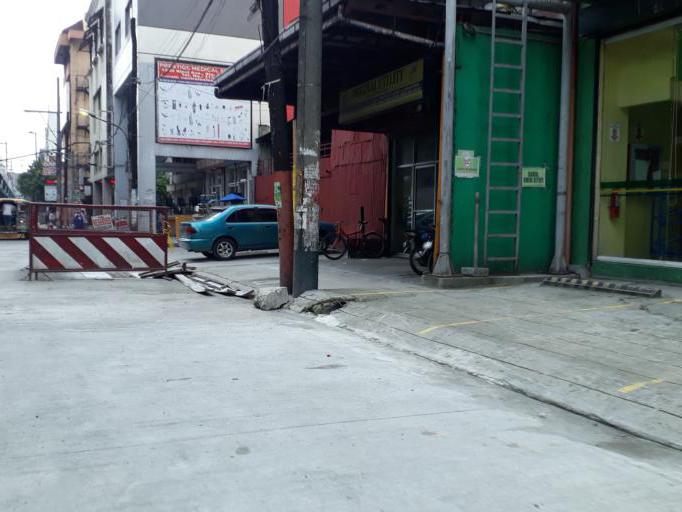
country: PH
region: Metro Manila
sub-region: City of Manila
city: Manila
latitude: 14.6081
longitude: 120.9824
